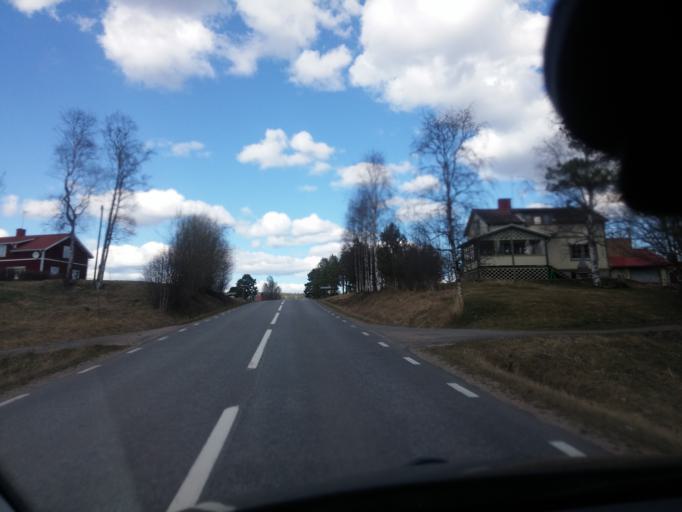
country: SE
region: Gaevleborg
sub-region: Ljusdals Kommun
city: Farila
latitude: 61.7895
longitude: 15.8300
